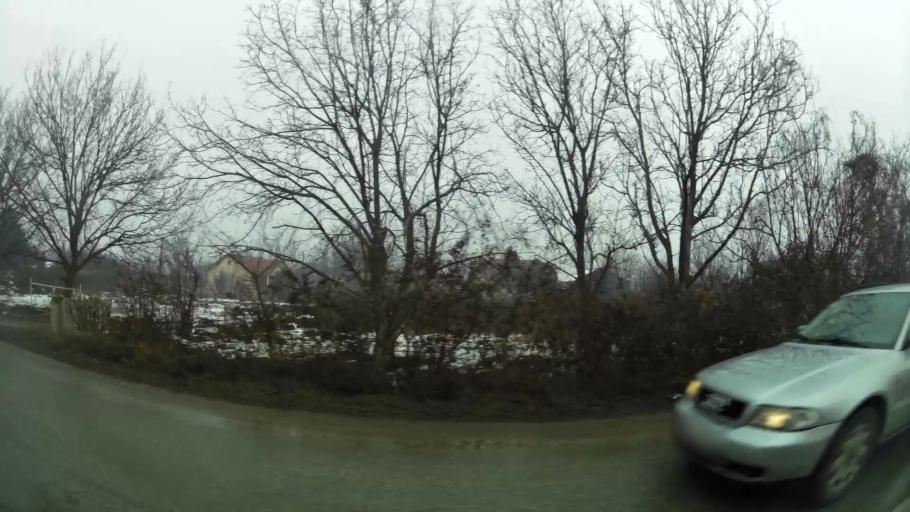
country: MK
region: Ilinden
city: Idrizovo
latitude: 41.9526
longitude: 21.5813
